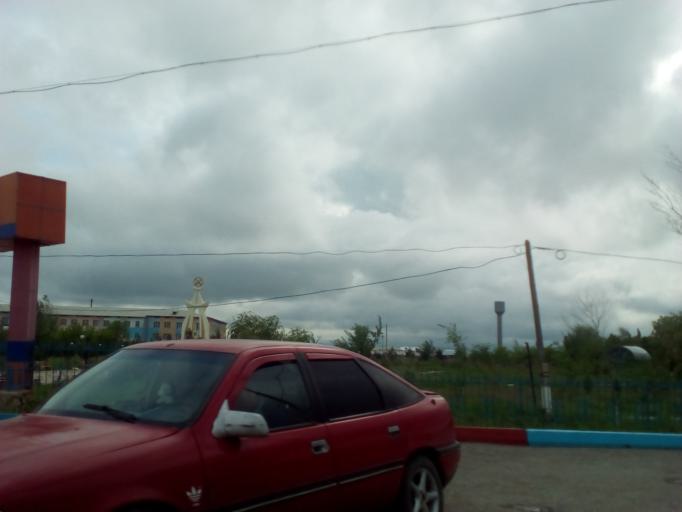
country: KZ
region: Ongtustik Qazaqstan
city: Sholaqqkorghan
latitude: 43.7562
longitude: 69.1910
